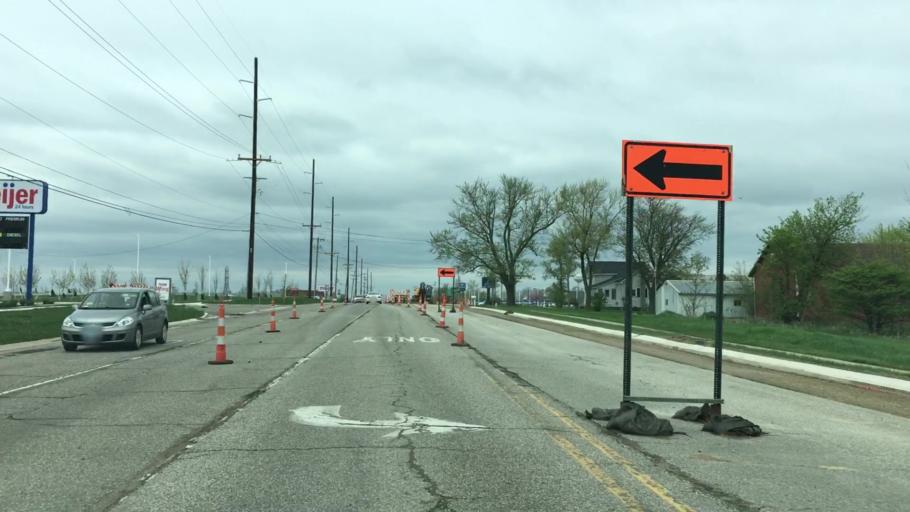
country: US
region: Michigan
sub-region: Ottawa County
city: Hudsonville
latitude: 42.8409
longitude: -85.8618
